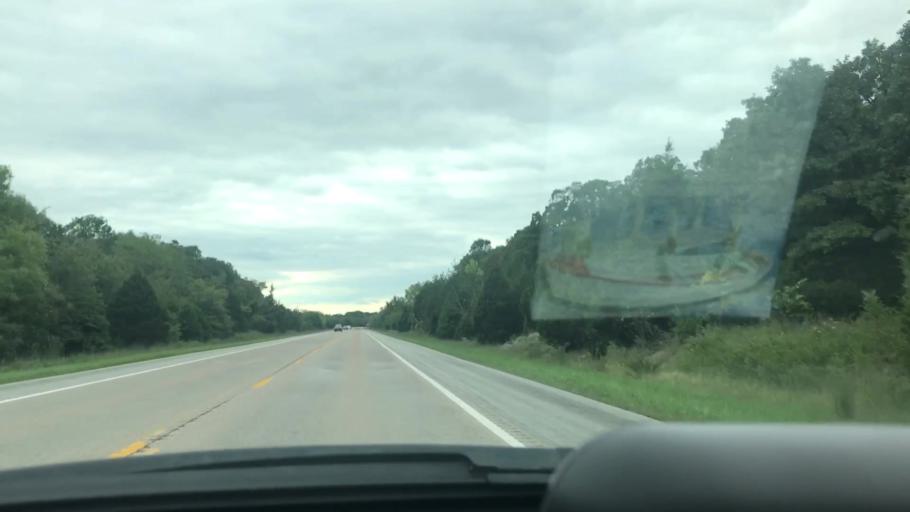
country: US
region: Missouri
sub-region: Benton County
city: Warsaw
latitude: 38.2095
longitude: -93.3342
